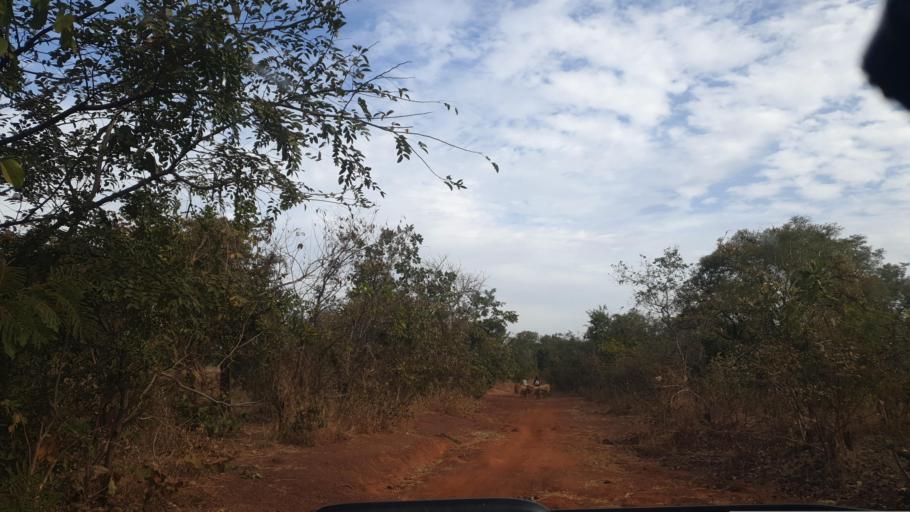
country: ML
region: Sikasso
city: Yanfolila
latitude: 11.4022
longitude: -8.0149
